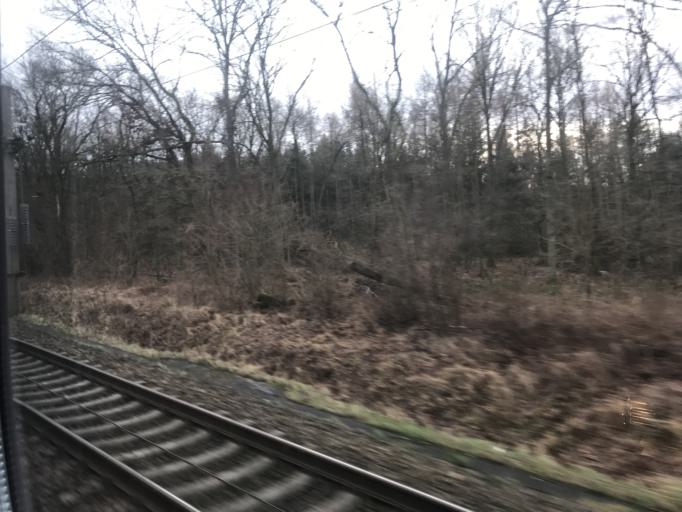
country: DE
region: Lower Saxony
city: Gifhorn
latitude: 52.4518
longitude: 10.5621
